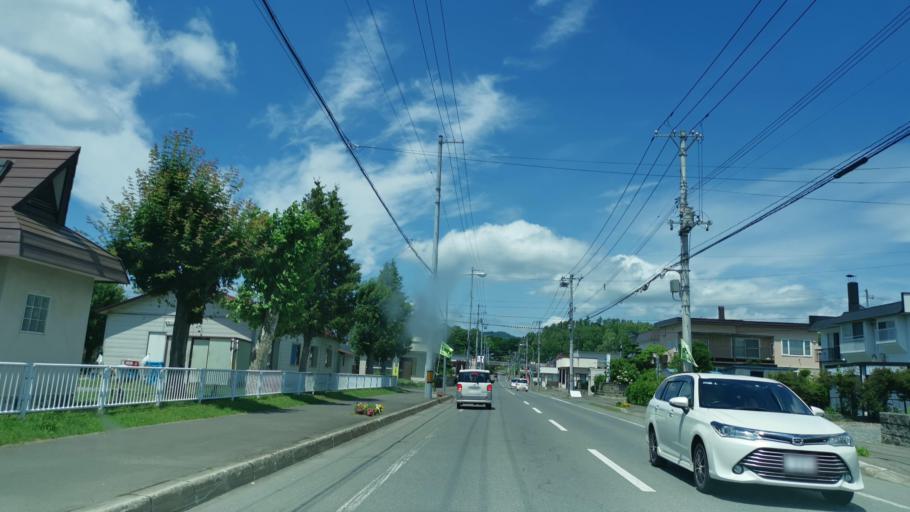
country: JP
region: Hokkaido
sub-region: Asahikawa-shi
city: Asahikawa
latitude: 43.7947
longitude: 142.3321
